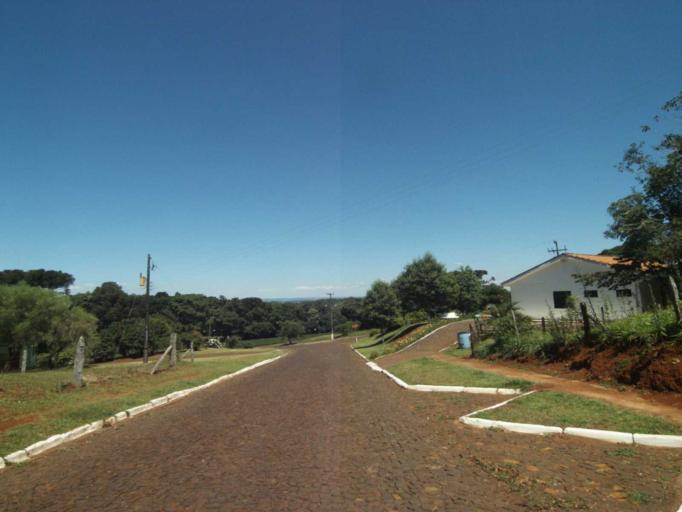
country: BR
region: Parana
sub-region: Laranjeiras Do Sul
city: Laranjeiras do Sul
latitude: -25.3871
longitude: -52.2120
